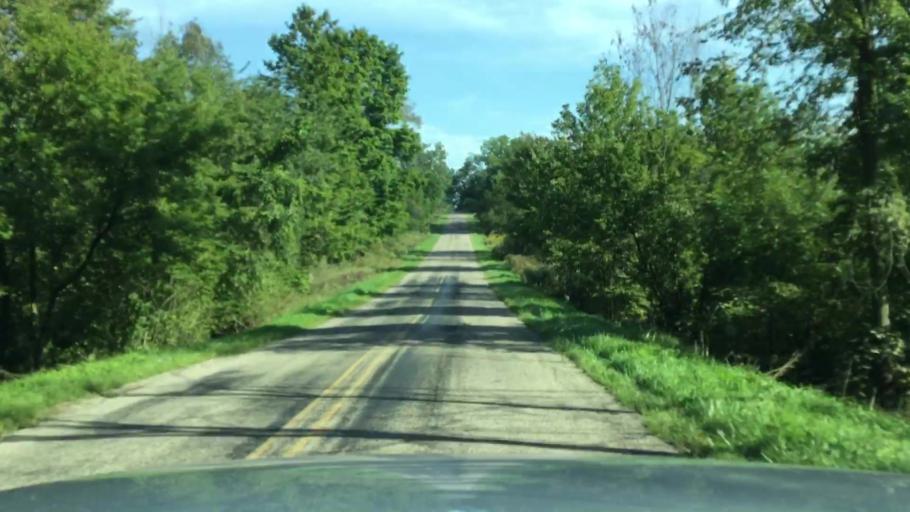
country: US
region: Michigan
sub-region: Lenawee County
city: Hudson
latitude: 41.8777
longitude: -84.4201
